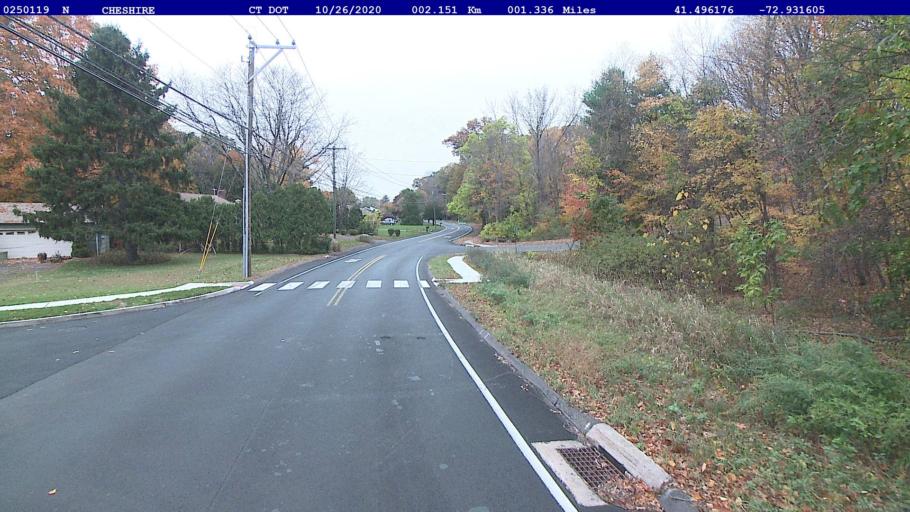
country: US
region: Connecticut
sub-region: New Haven County
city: Cheshire
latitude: 41.4962
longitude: -72.9315
